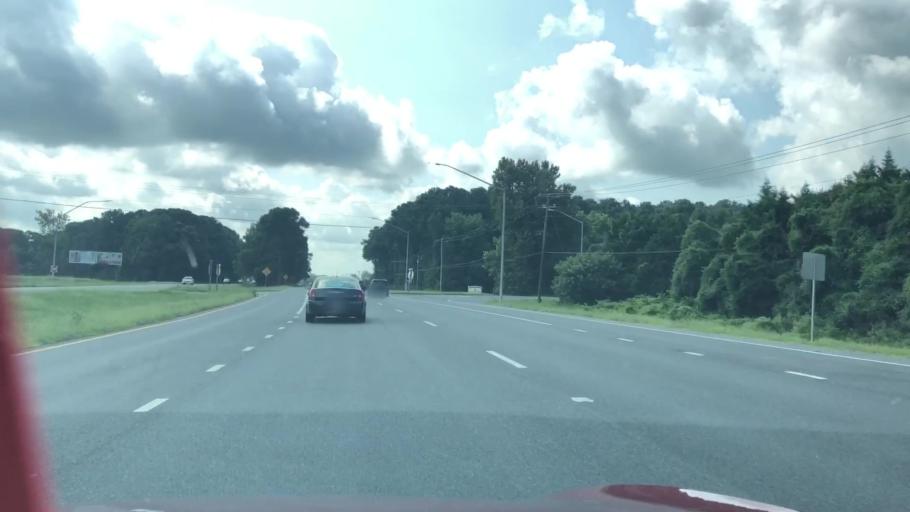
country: US
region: Maryland
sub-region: Somerset County
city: Princess Anne
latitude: 38.1922
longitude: -75.6964
